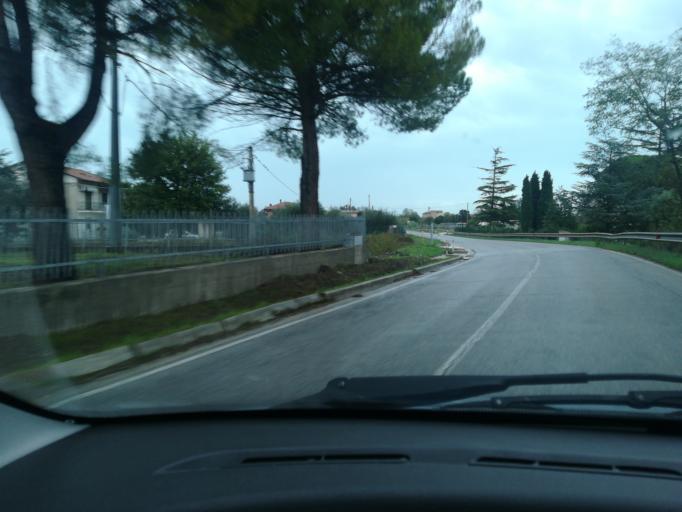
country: IT
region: The Marches
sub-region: Provincia di Macerata
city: Trodica
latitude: 43.2761
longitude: 13.6068
